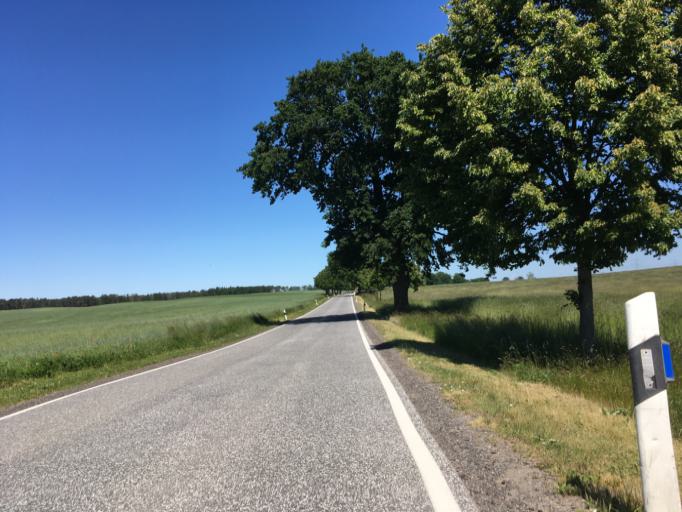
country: DE
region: Brandenburg
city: Zehdenick
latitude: 52.9050
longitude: 13.2554
